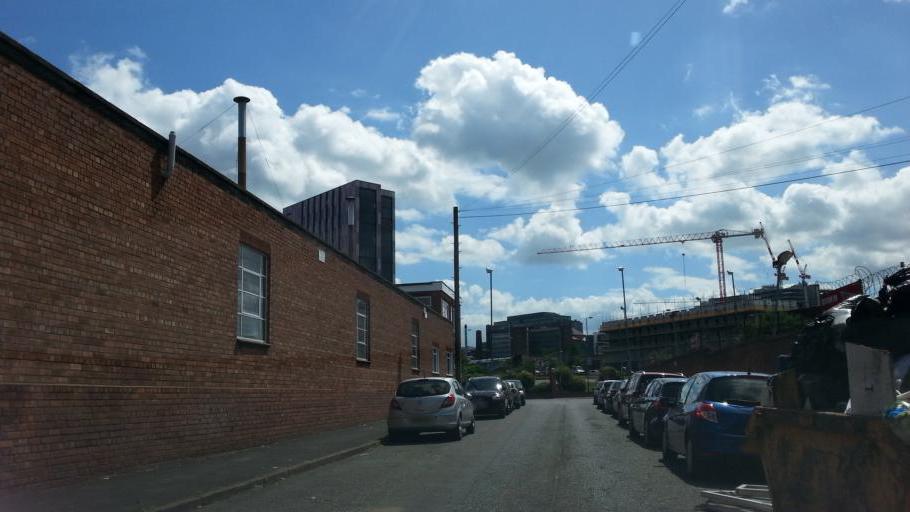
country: GB
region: England
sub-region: City and Borough of Birmingham
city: Birmingham
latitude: 52.4908
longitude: -1.8937
